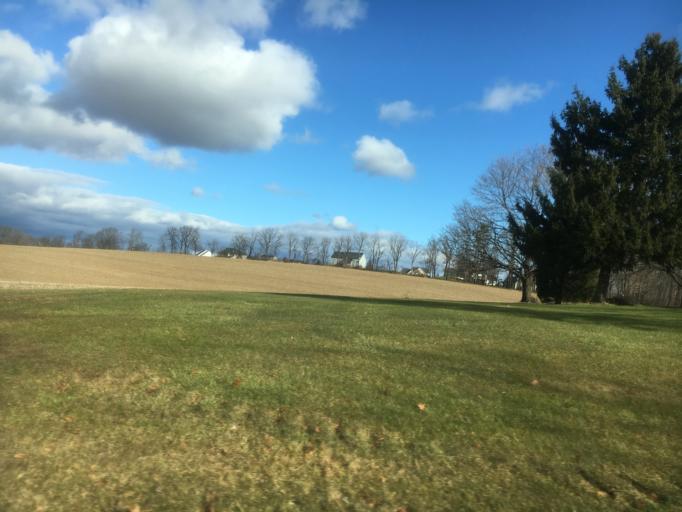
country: US
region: Pennsylvania
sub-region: Lehigh County
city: Egypt
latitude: 40.6968
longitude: -75.5663
